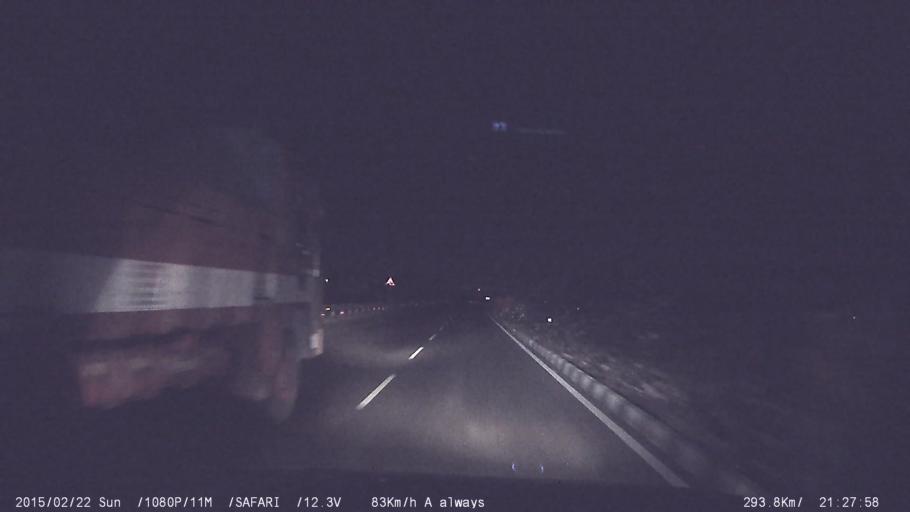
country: IN
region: Tamil Nadu
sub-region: Karur
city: Karur
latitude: 10.9209
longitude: 78.0448
